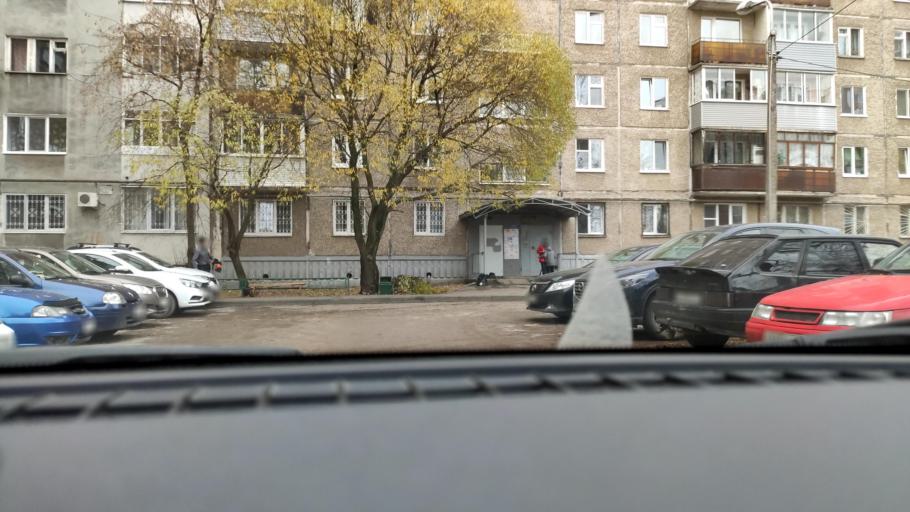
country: RU
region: Perm
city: Kondratovo
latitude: 57.9982
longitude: 56.1727
